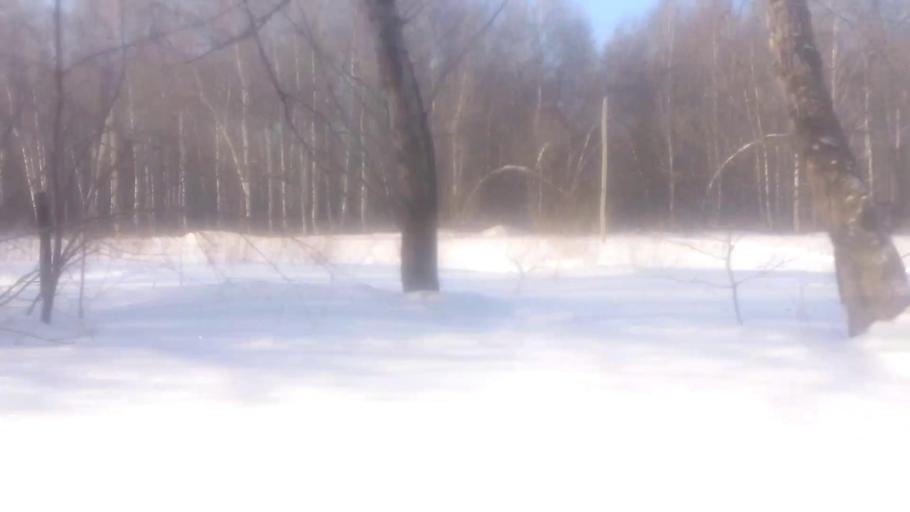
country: RU
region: Altai Krai
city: Novosilikatnyy
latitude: 53.3721
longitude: 83.6623
